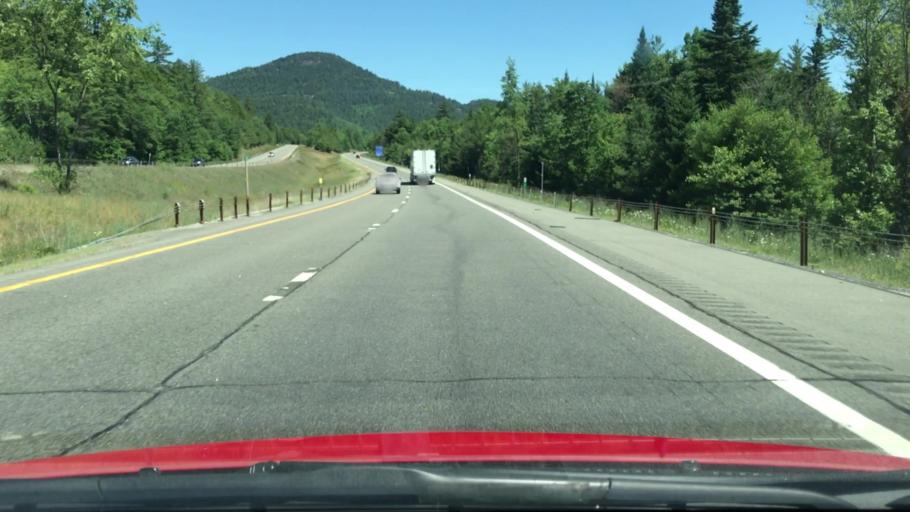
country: US
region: New York
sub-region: Essex County
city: Mineville
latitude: 43.9814
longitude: -73.7232
